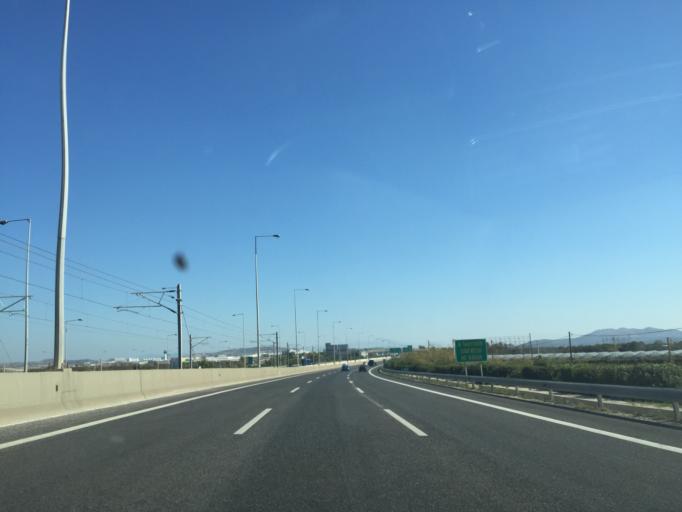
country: GR
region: Attica
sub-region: Nomarchia Anatolikis Attikis
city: Markopoulo
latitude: 37.9123
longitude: 23.9114
